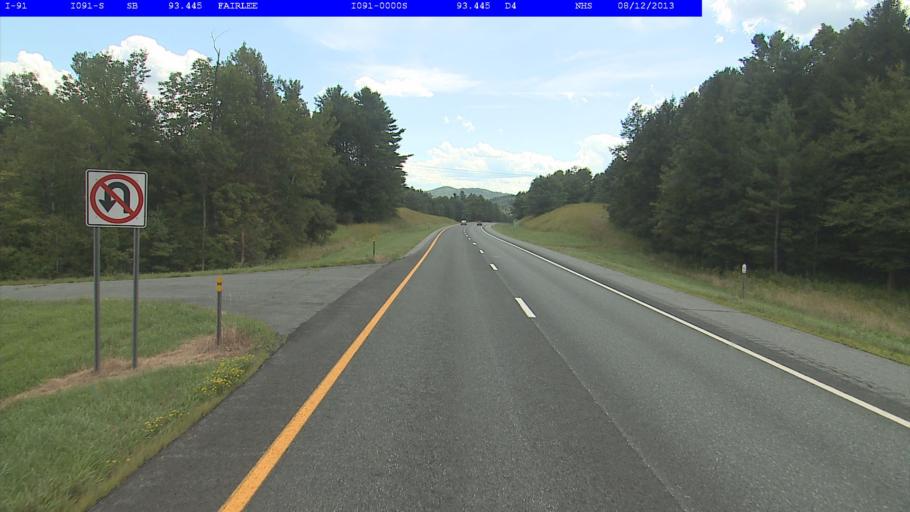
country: US
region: New Hampshire
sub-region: Grafton County
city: Orford
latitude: 43.9253
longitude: -72.1339
